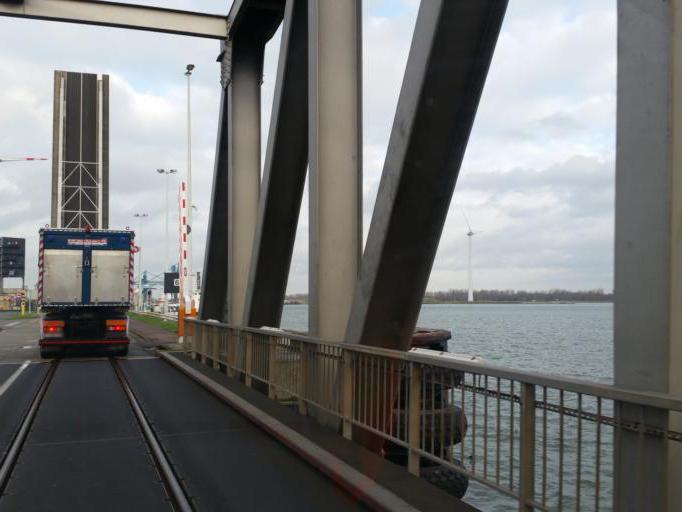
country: BE
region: Flanders
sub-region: Provincie Antwerpen
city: Stabroek
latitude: 51.3439
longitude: 4.2901
